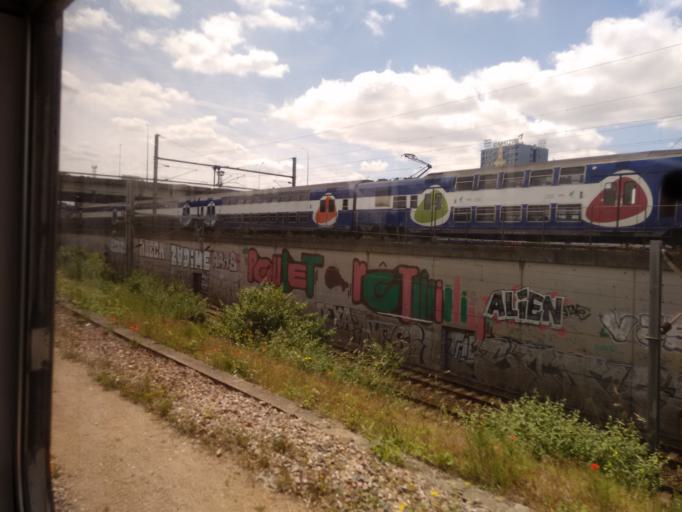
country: FR
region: Ile-de-France
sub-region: Paris
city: Saint-Ouen
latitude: 48.9022
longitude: 2.3543
